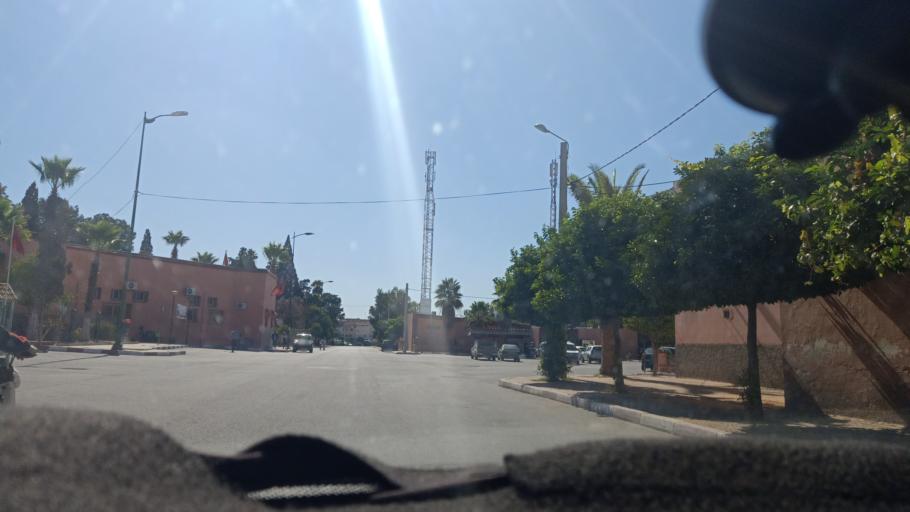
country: MA
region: Doukkala-Abda
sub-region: Safi
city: Youssoufia
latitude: 32.2447
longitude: -8.5334
